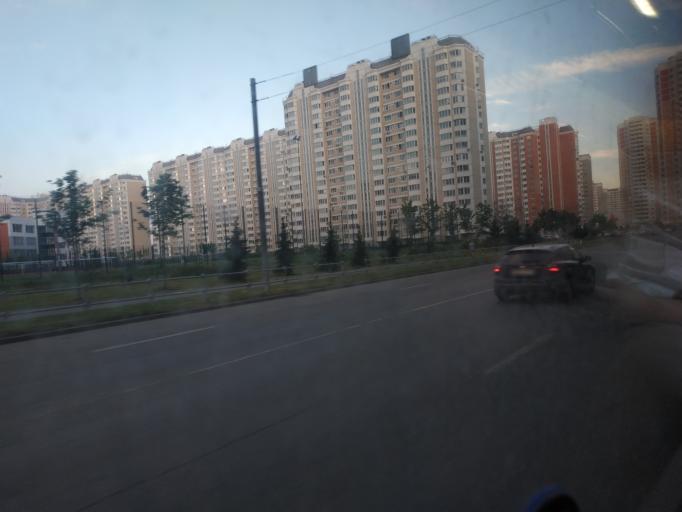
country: RU
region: Moskovskaya
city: Moskovskiy
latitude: 55.6048
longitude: 37.3630
